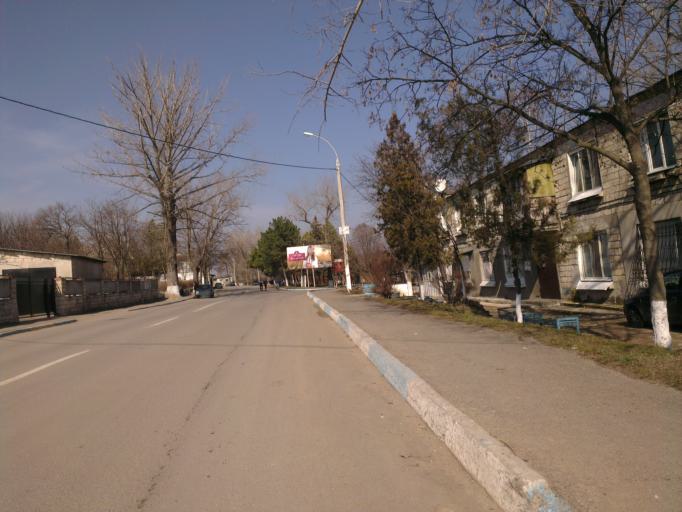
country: MD
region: Chisinau
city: Cricova
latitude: 47.1423
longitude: 28.8641
